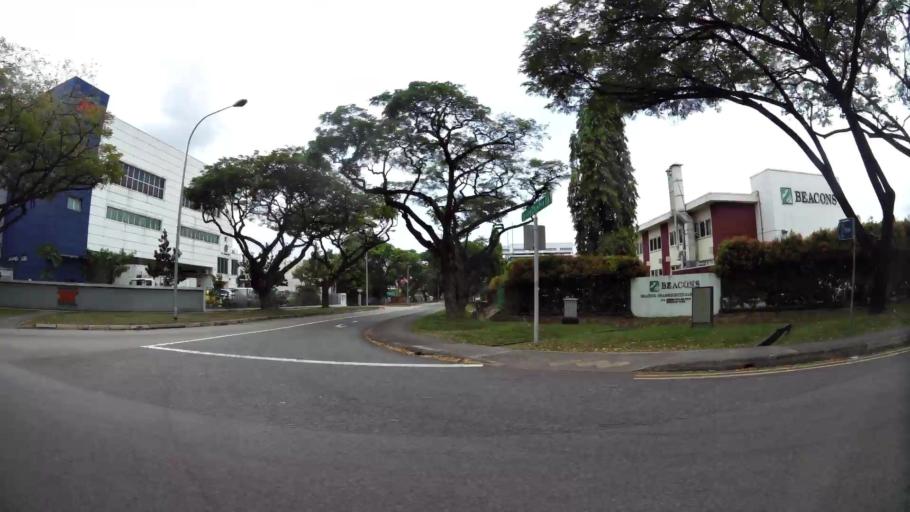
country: SG
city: Singapore
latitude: 1.3300
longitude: 103.7151
